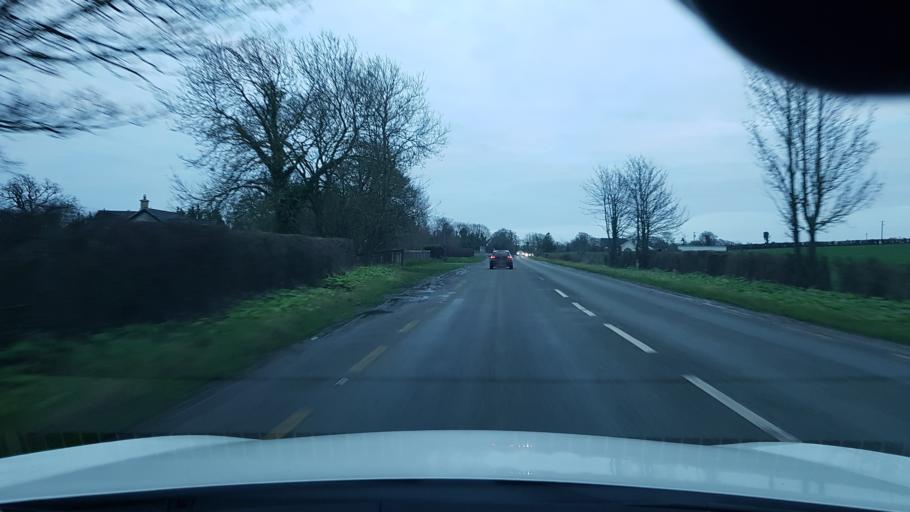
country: IE
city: Kentstown
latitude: 53.5912
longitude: -6.6004
